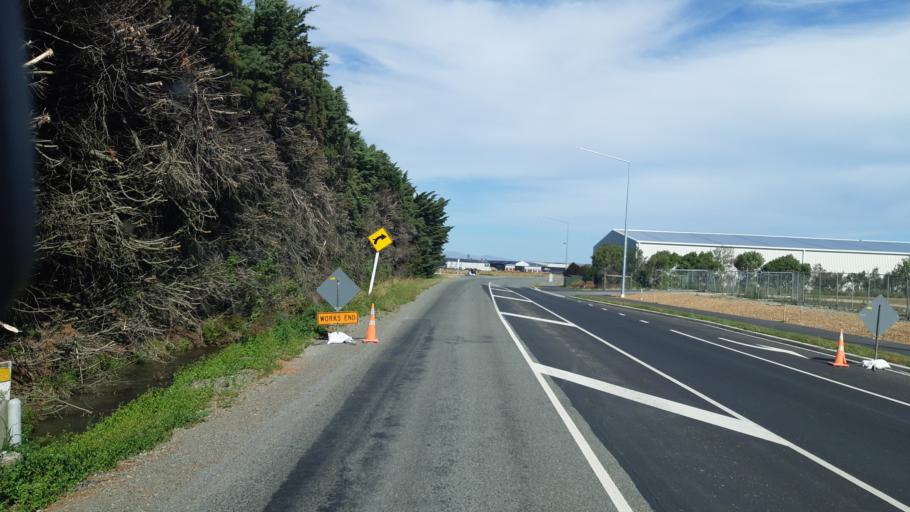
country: NZ
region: Canterbury
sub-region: Selwyn District
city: Rolleston
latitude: -43.5739
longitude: 172.3778
